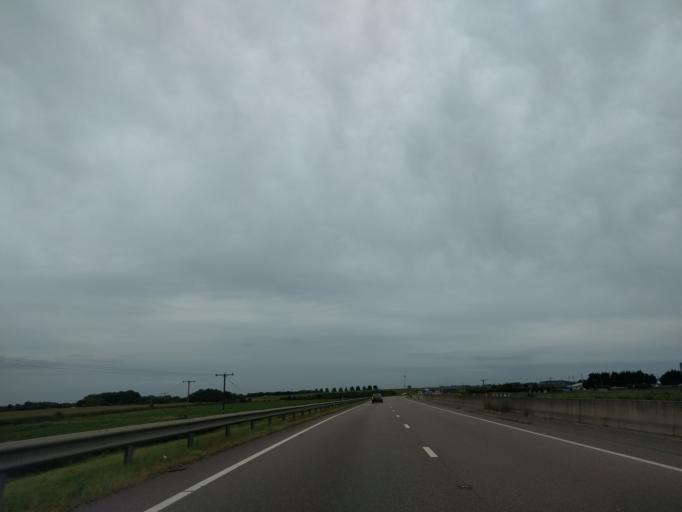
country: GB
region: England
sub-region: Nottinghamshire
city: Farndon
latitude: 53.0585
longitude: -0.8384
